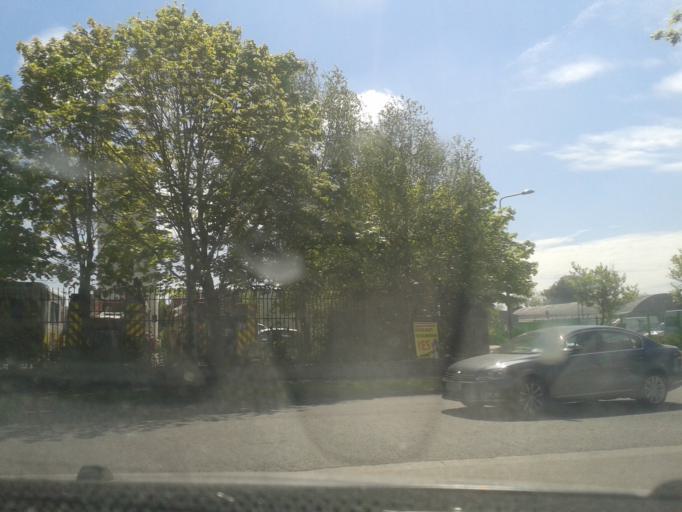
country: IE
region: Leinster
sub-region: Fingal County
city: Blanchardstown
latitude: 53.3850
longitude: -6.3964
